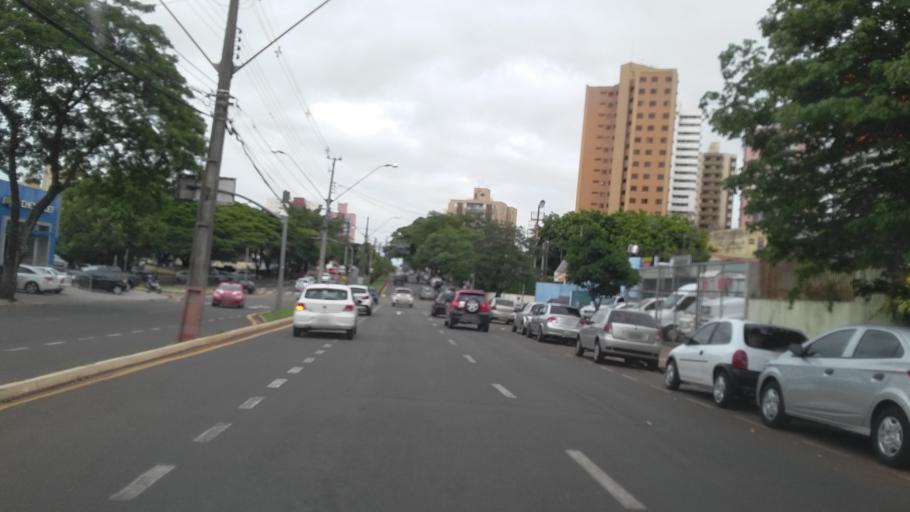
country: BR
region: Parana
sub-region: Londrina
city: Londrina
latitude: -23.3198
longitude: -51.1619
